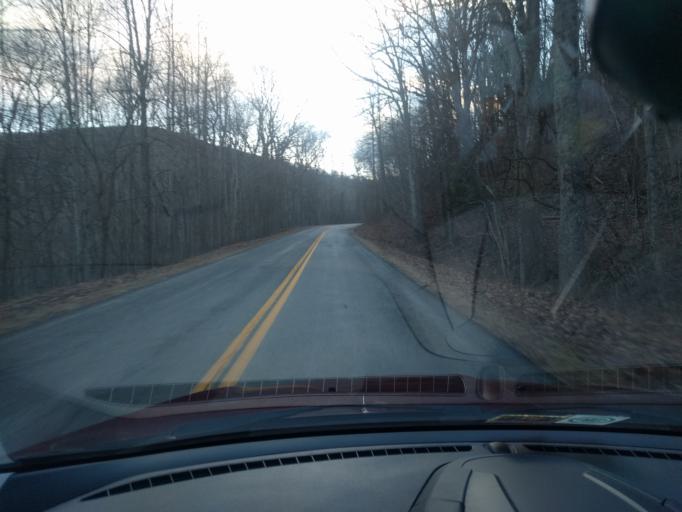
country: US
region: Virginia
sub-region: Botetourt County
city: Buchanan
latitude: 37.4609
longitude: -79.6322
